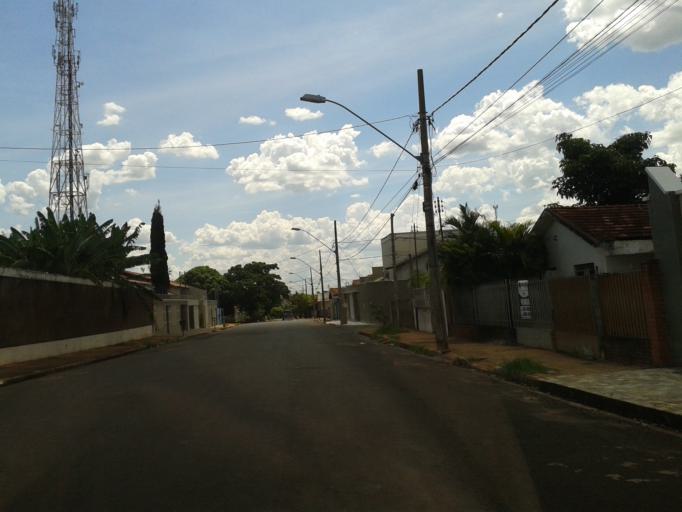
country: BR
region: Minas Gerais
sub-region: Ituiutaba
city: Ituiutaba
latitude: -18.9855
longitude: -49.4652
